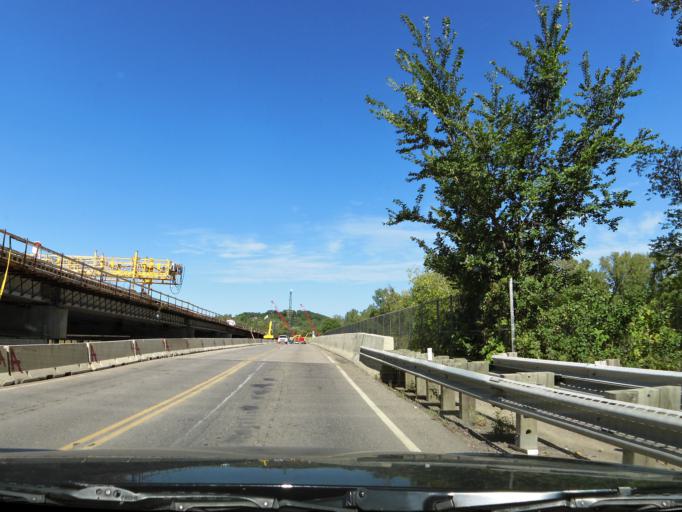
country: US
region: Minnesota
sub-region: Scott County
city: Shakopee
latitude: 44.8074
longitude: -93.5342
